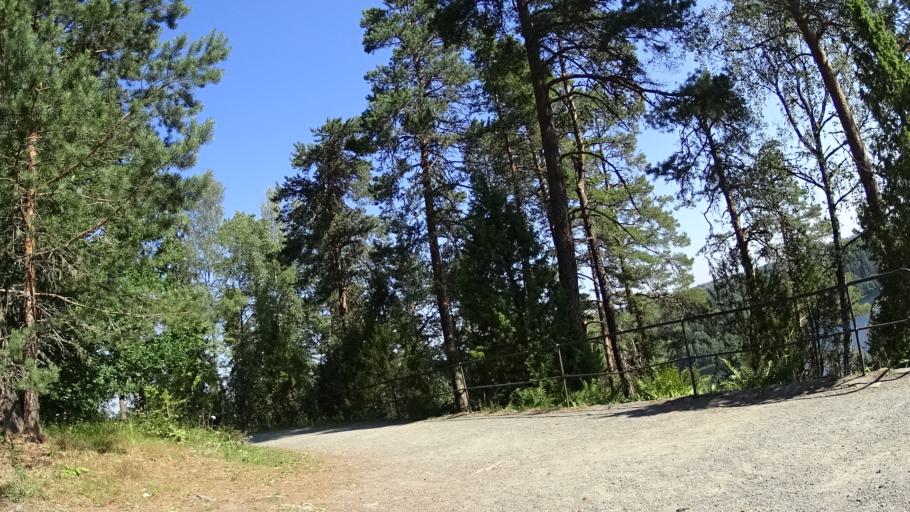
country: FI
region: Haeme
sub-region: Haemeenlinna
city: Haemeenlinna
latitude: 61.0223
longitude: 24.4701
